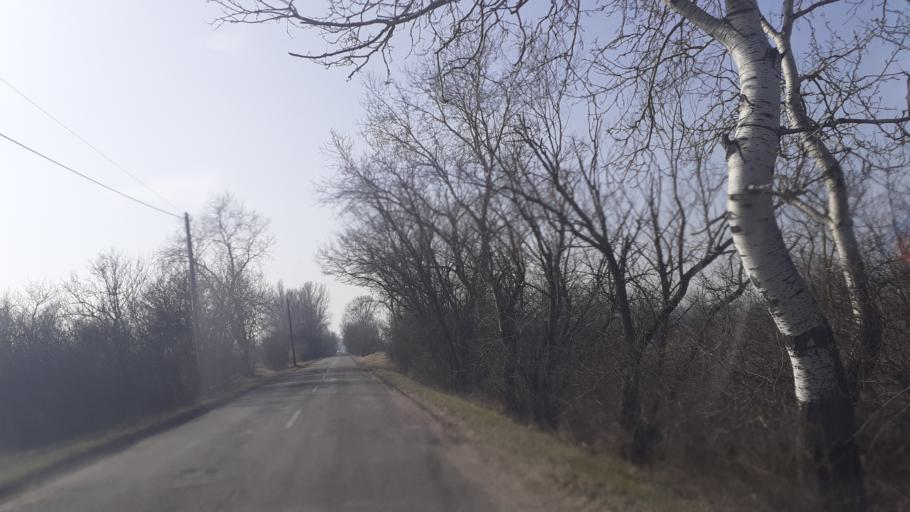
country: HU
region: Pest
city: Orkeny
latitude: 47.0723
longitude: 19.3591
